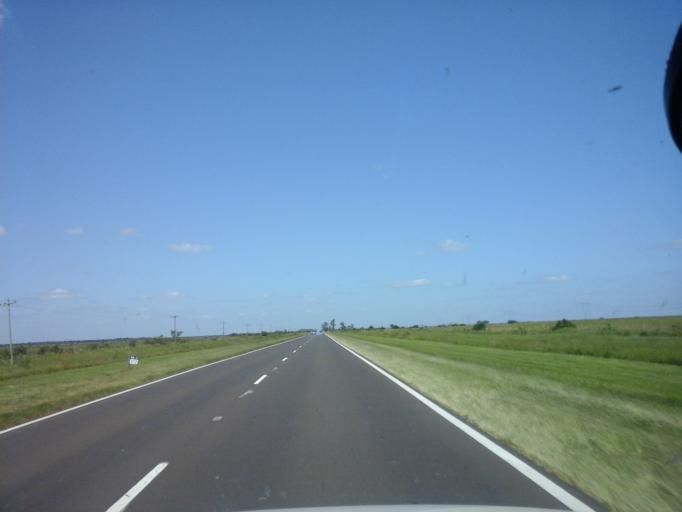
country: AR
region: Corrientes
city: Ita Ibate
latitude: -27.4588
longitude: -57.4397
